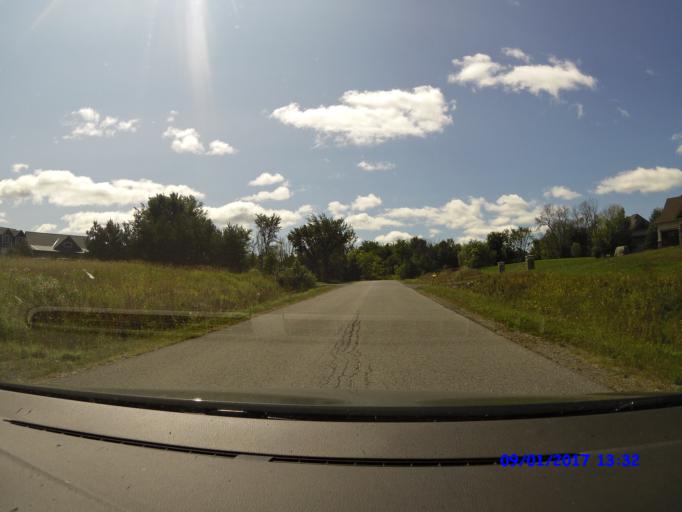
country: CA
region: Ontario
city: Bells Corners
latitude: 45.3554
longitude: -75.9939
